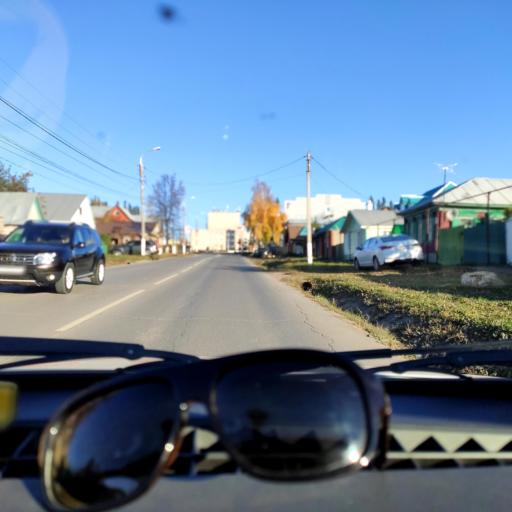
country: RU
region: Bashkortostan
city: Blagoveshchensk
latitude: 55.0442
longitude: 55.9599
